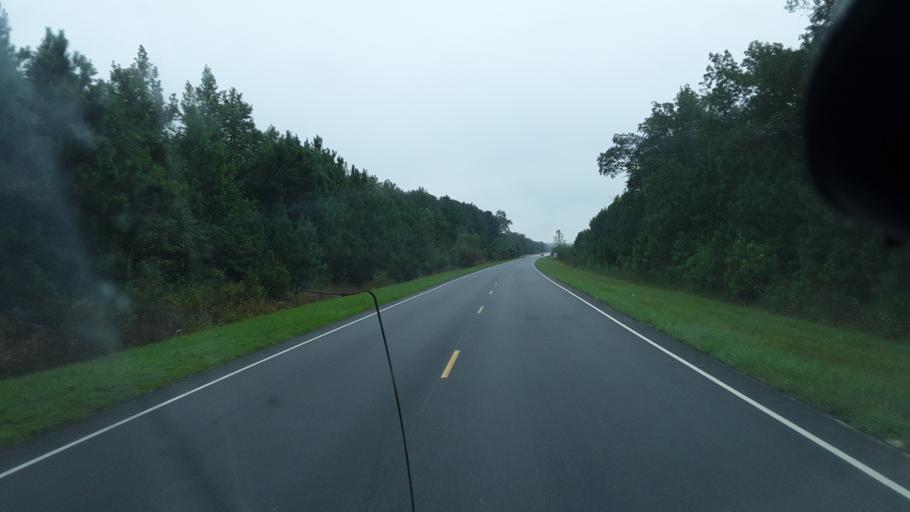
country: US
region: South Carolina
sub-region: Florence County
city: Johnsonville
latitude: 33.9008
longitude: -79.4398
